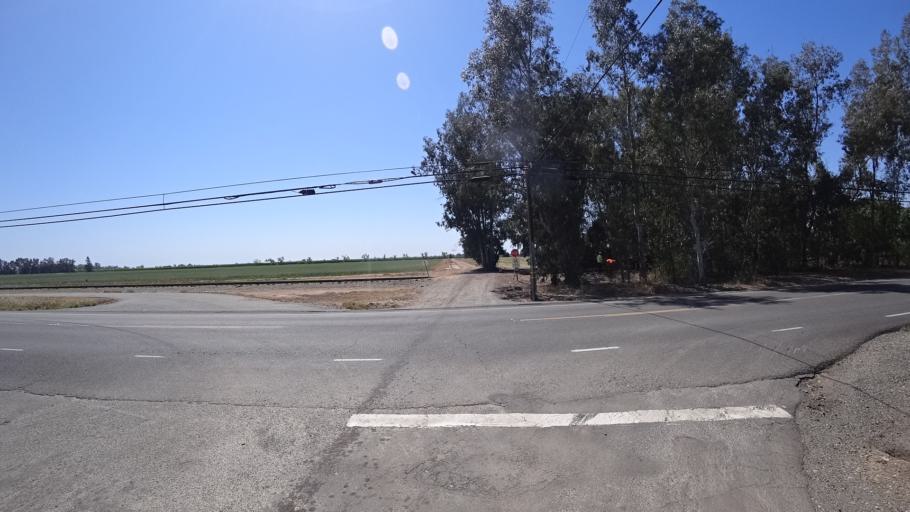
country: US
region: California
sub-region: Glenn County
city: Orland
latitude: 39.7690
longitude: -122.1783
